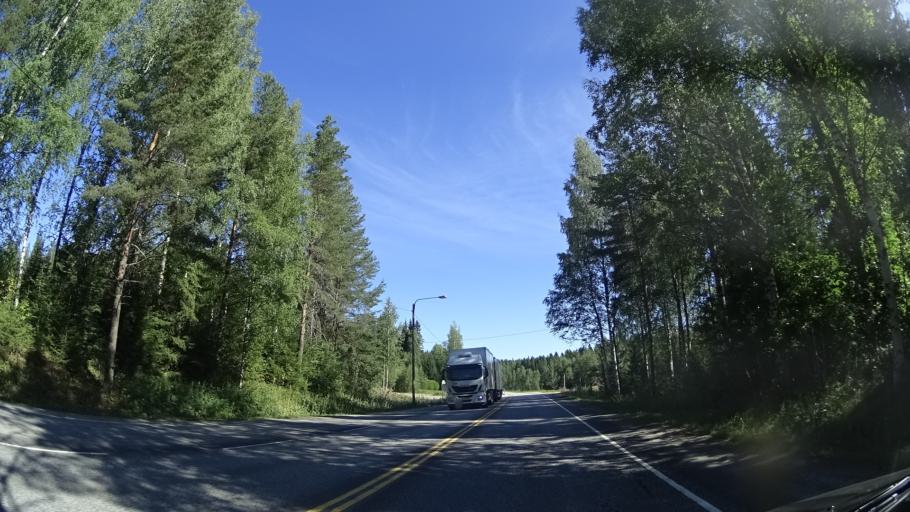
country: FI
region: Central Finland
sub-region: AEaenekoski
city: AEaenekoski
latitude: 62.8273
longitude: 25.8126
